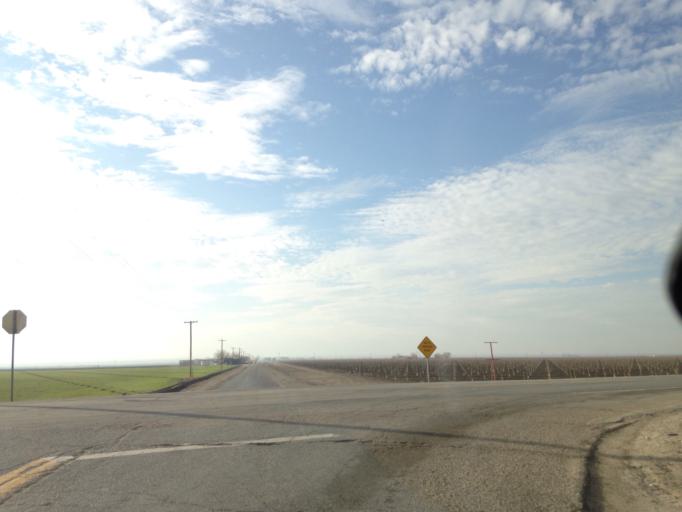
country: US
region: California
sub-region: Kern County
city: Buttonwillow
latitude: 35.4417
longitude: -119.5500
